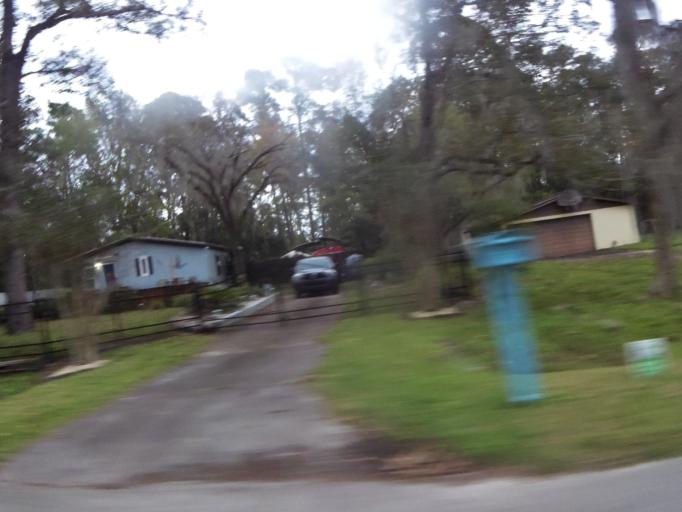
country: US
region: Florida
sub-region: Duval County
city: Jacksonville
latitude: 30.2602
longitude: -81.5814
